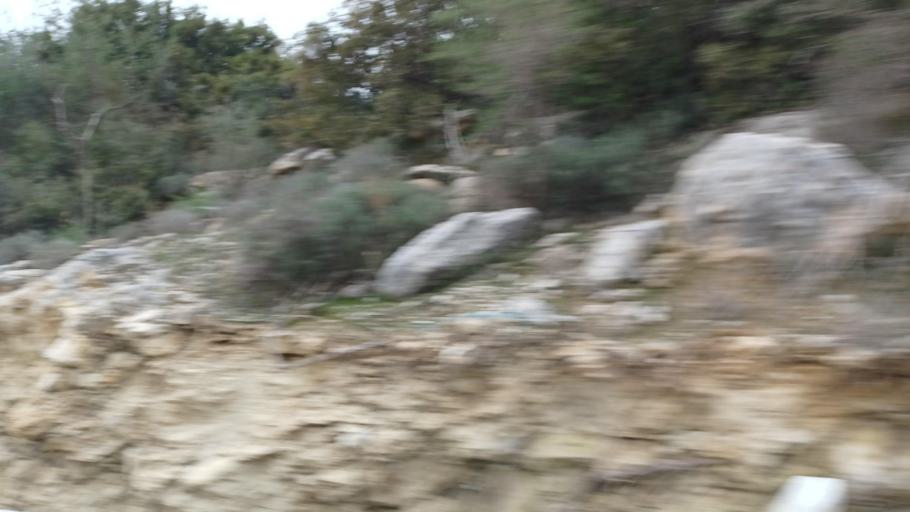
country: CY
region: Limassol
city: Pissouri
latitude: 34.7172
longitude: 32.7408
